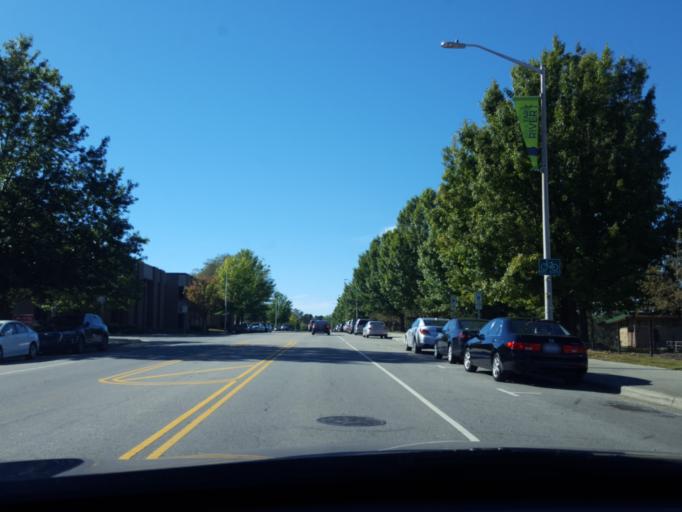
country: US
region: North Carolina
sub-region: Pitt County
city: Greenville
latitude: 35.6148
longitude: -77.3691
